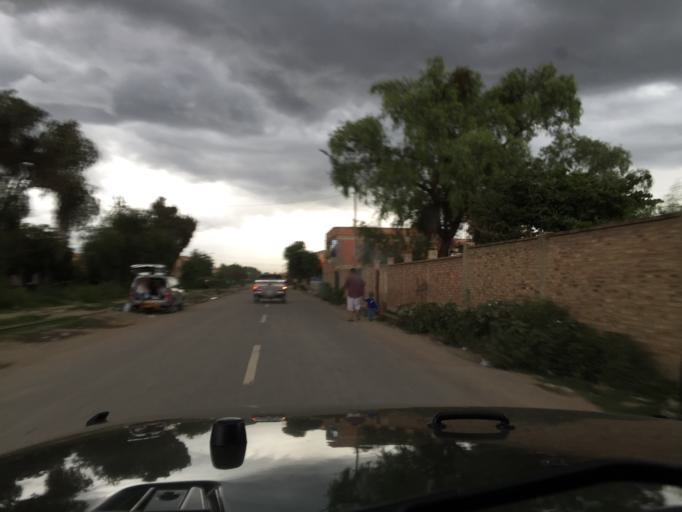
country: BO
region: Cochabamba
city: Cochabamba
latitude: -17.3999
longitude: -66.2064
